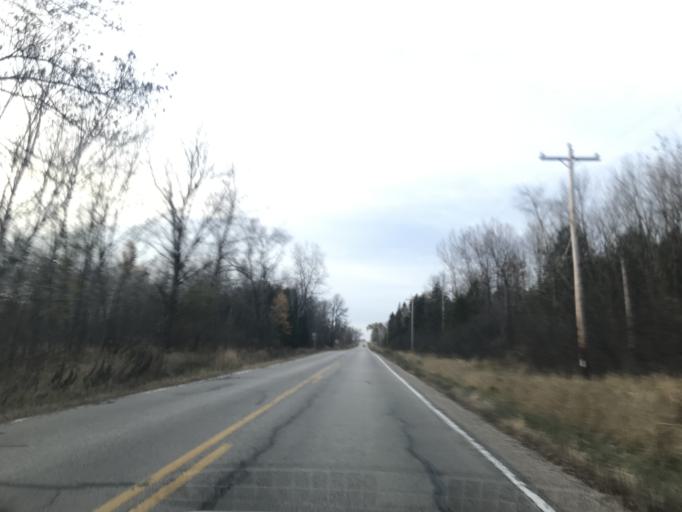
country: US
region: Wisconsin
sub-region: Marinette County
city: Peshtigo
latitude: 45.1053
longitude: -87.7994
